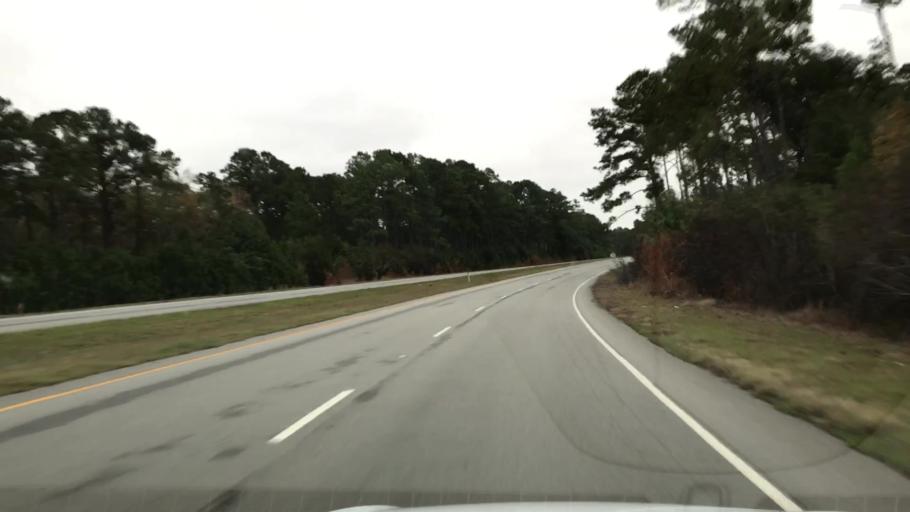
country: US
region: South Carolina
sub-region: Georgetown County
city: Georgetown
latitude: 33.1802
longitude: -79.4122
